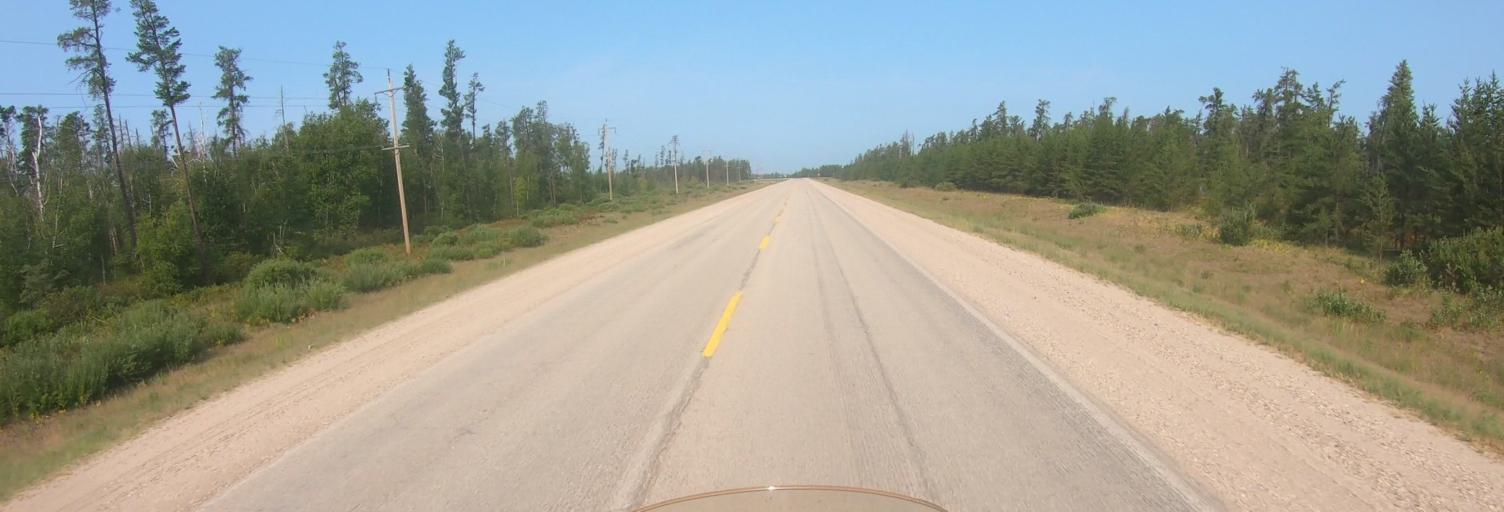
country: US
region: Minnesota
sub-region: Roseau County
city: Roseau
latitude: 49.0852
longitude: -95.8811
